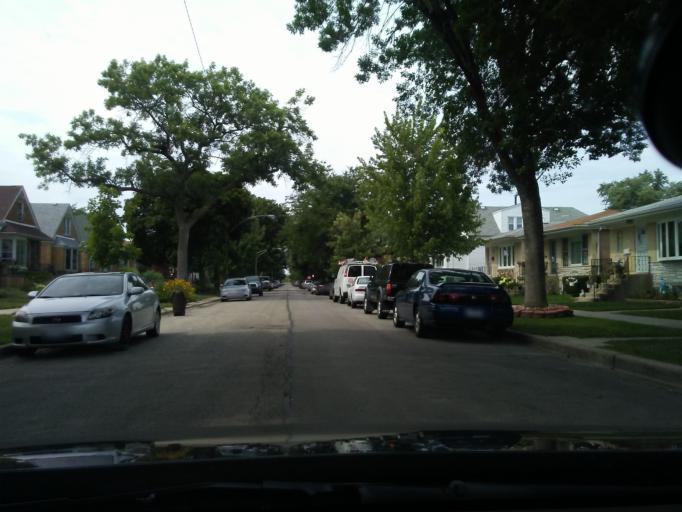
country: US
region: Illinois
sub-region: Cook County
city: Harwood Heights
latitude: 41.9778
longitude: -87.7836
